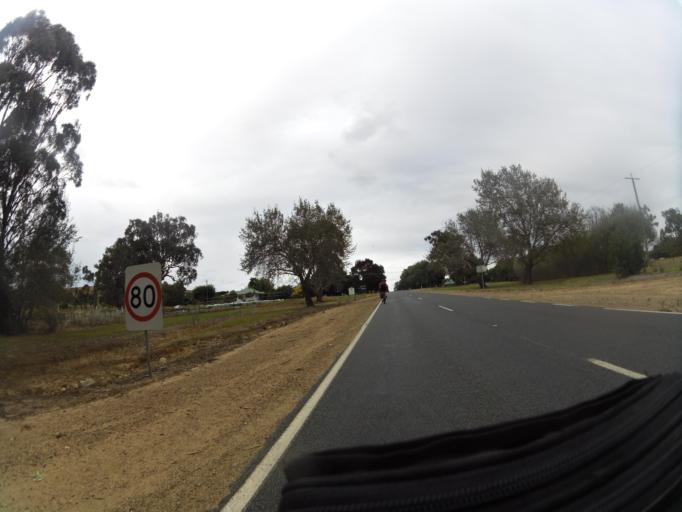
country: AU
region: New South Wales
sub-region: Snowy River
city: Jindabyne
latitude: -36.1864
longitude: 147.9181
